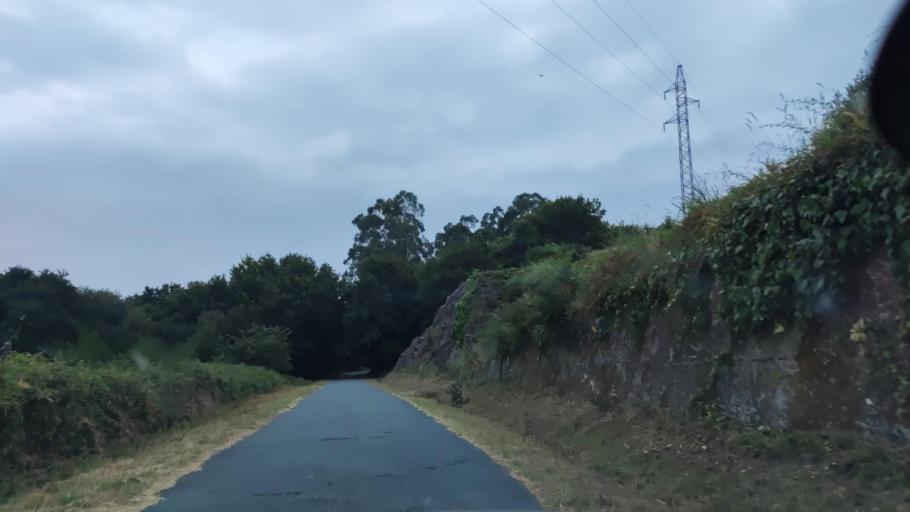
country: ES
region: Galicia
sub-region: Provincia de Pontevedra
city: Catoira
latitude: 42.7085
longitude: -8.7225
